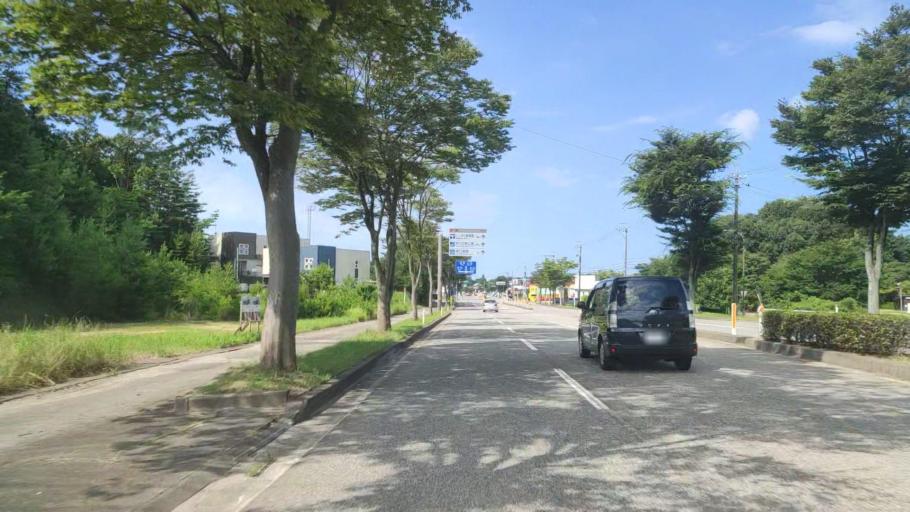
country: JP
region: Ishikawa
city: Matsuto
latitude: 36.4447
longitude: 136.5519
